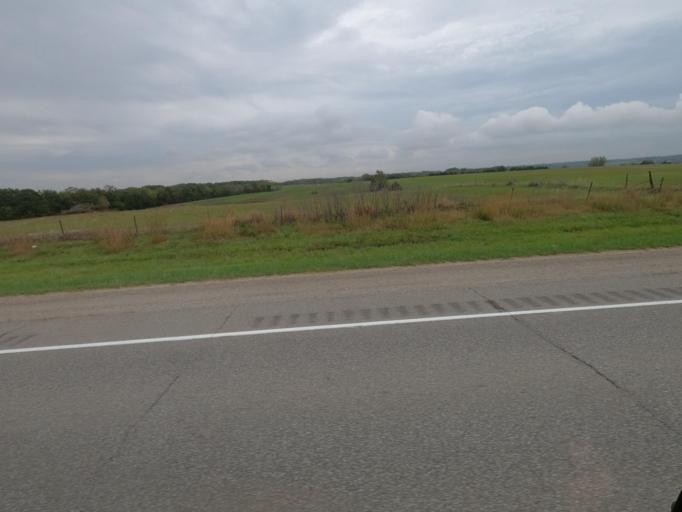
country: US
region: Iowa
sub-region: Van Buren County
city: Keosauqua
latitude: 40.8340
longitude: -91.9491
